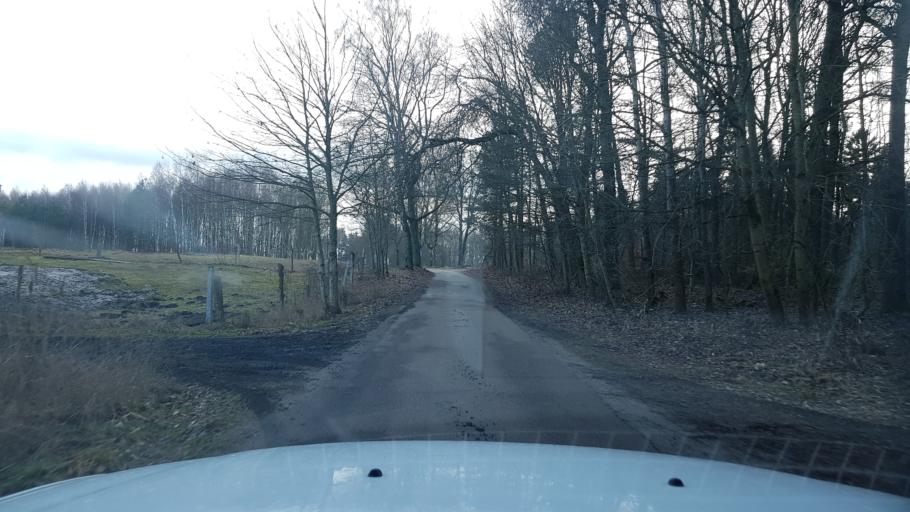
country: PL
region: West Pomeranian Voivodeship
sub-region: Powiat szczecinecki
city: Borne Sulinowo
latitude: 53.6276
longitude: 16.6127
